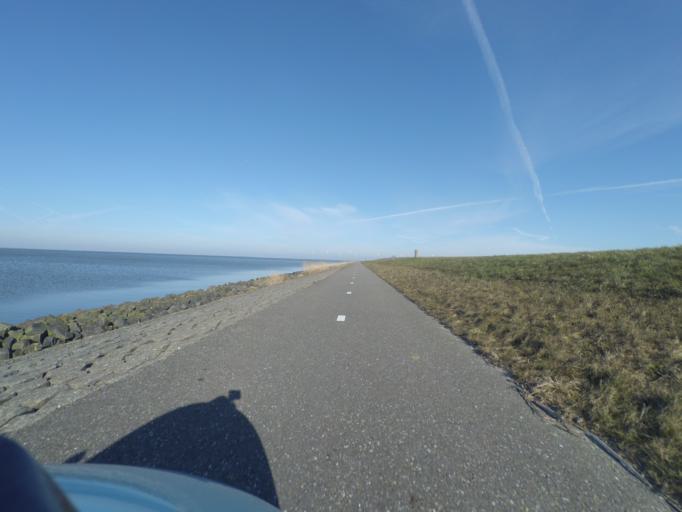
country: NL
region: North Holland
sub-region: Gemeente Naarden
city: Naarden
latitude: 52.3508
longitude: 5.1339
